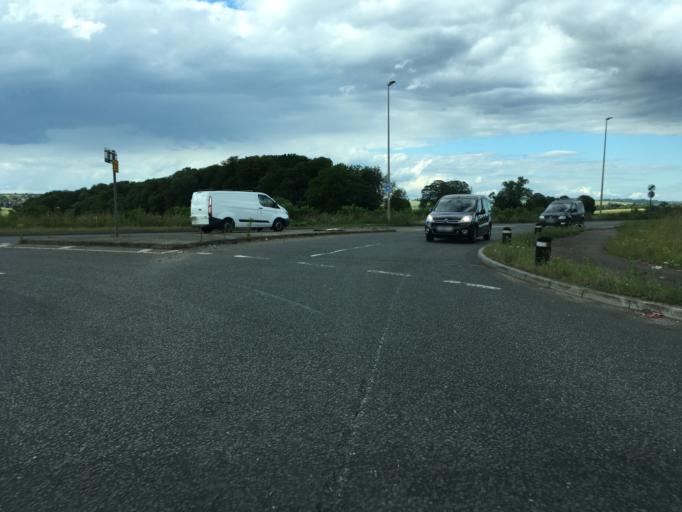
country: GB
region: England
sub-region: Buckinghamshire
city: Haddenham
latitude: 51.7763
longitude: -0.9474
